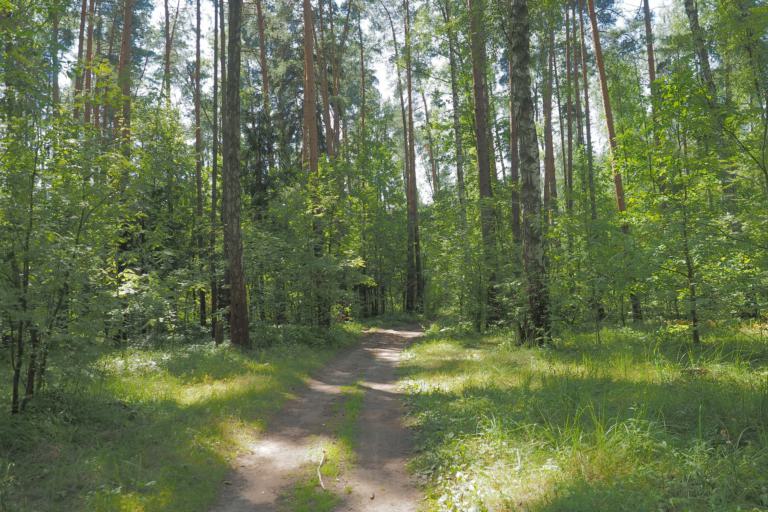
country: RU
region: Moskovskaya
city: Malyshevo
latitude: 55.5241
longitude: 38.3579
